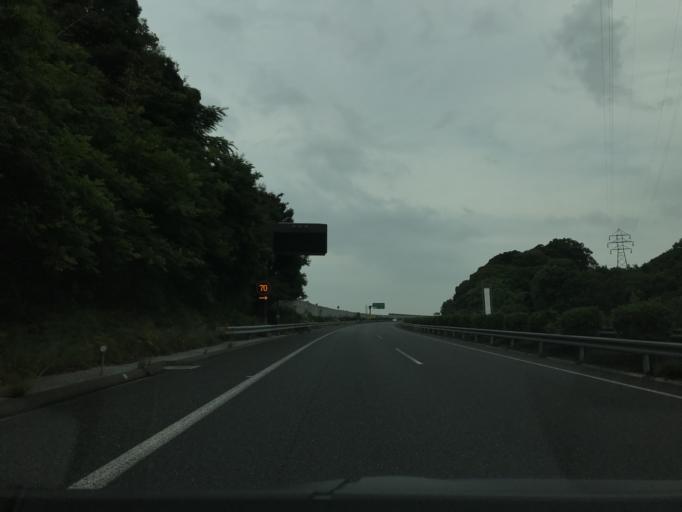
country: JP
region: Fukuoka
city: Kanda
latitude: 33.7989
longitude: 130.9589
